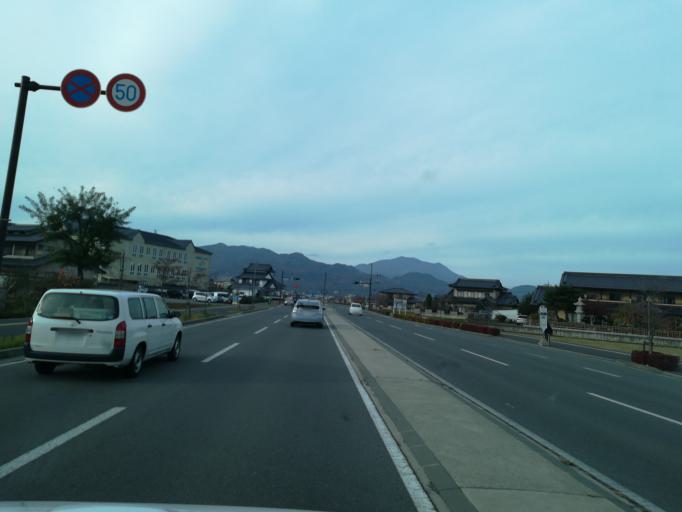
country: JP
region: Nagano
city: Nagano-shi
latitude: 36.5965
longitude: 138.1827
